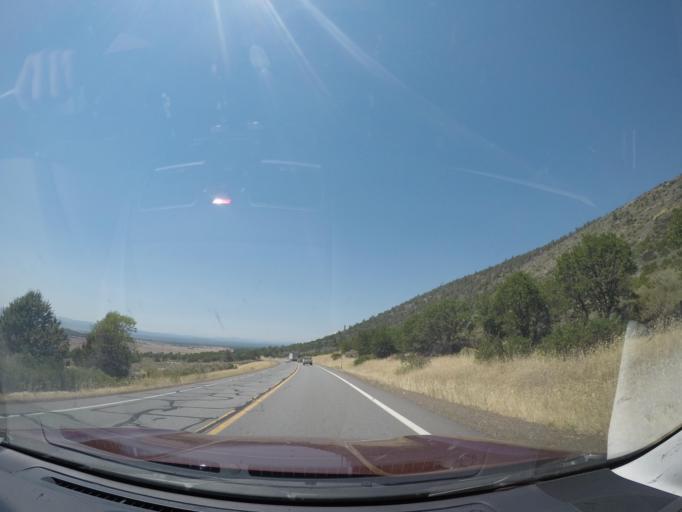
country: US
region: California
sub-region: Shasta County
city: Burney
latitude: 41.0903
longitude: -121.2692
